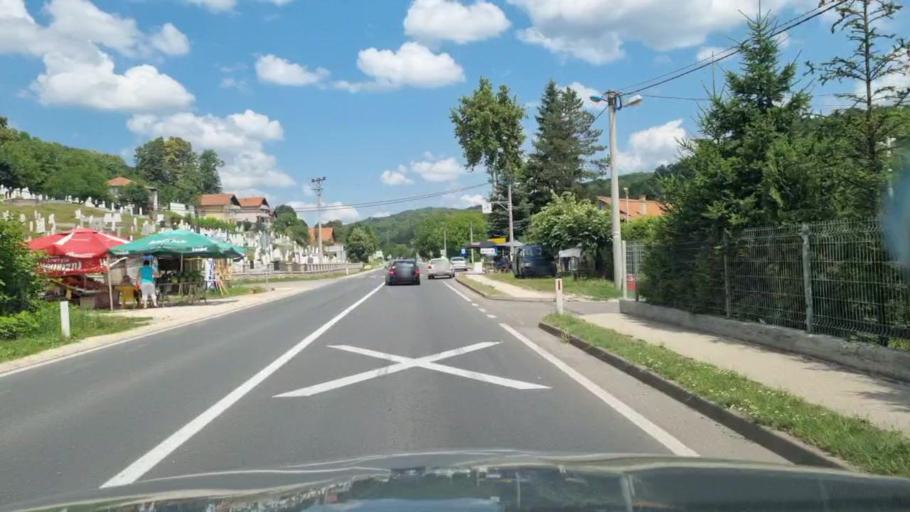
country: BA
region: Federation of Bosnia and Herzegovina
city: Mramor
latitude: 44.5792
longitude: 18.5841
